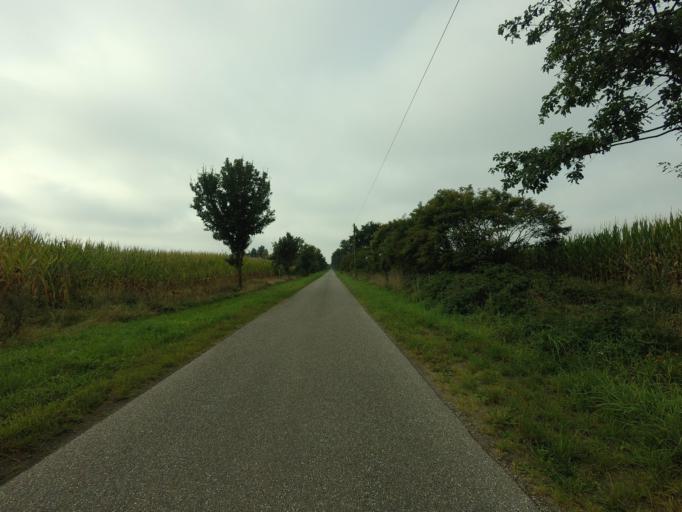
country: DE
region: Lower Saxony
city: Wielen
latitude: 52.5191
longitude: 6.7302
